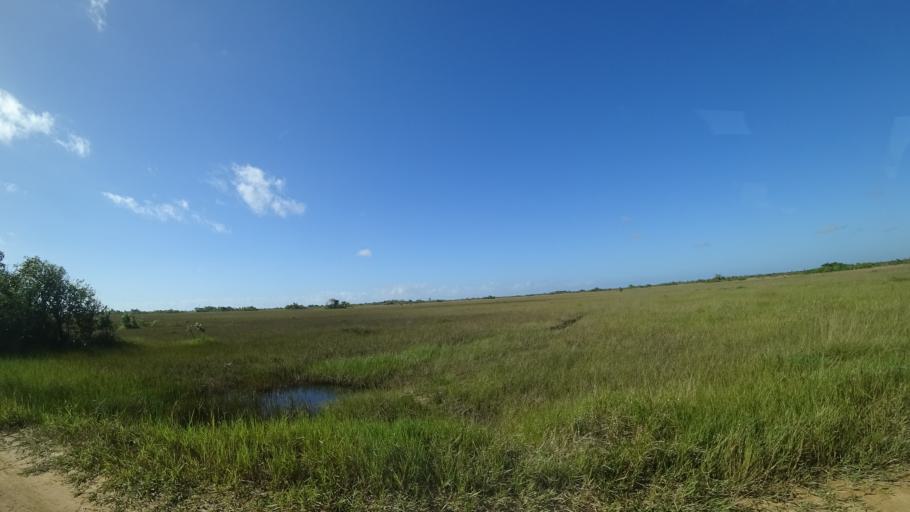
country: MZ
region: Sofala
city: Beira
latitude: -19.6938
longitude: 35.0369
